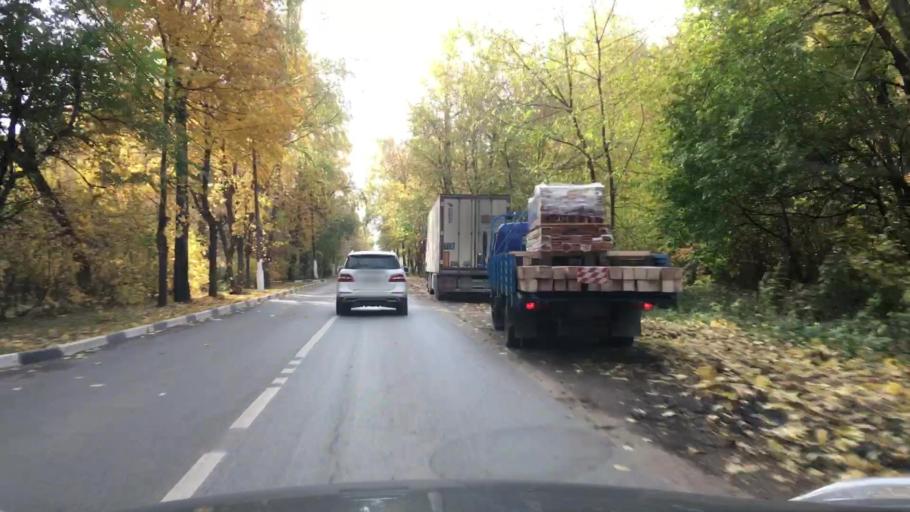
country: RU
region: Moskovskaya
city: Balashikha
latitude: 55.8034
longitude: 37.9273
